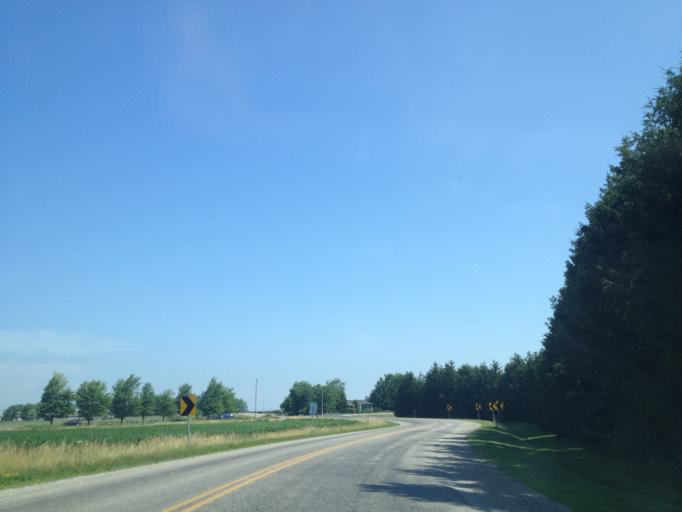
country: CA
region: Ontario
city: London
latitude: 43.1965
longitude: -81.2415
